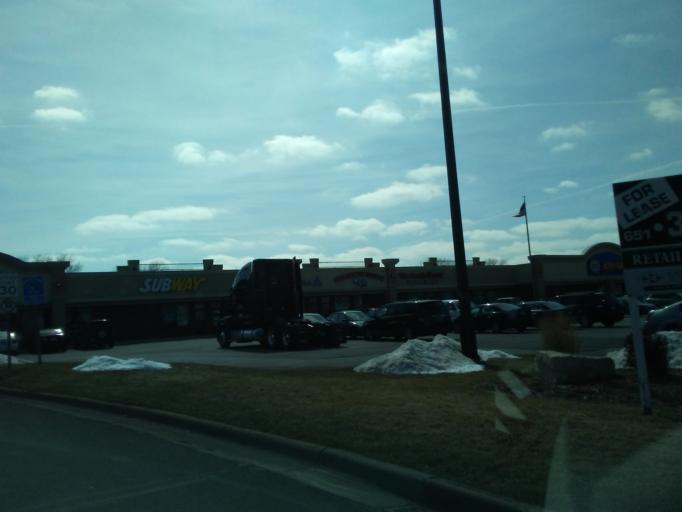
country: US
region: Minnesota
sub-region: Dakota County
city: Eagan
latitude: 44.8334
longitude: -93.1696
